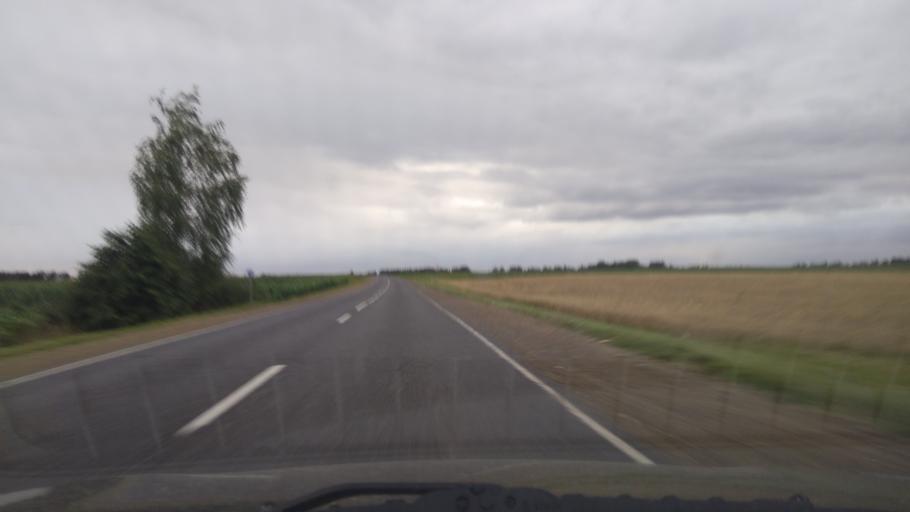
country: BY
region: Brest
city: Byaroza
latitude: 52.4302
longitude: 24.9806
